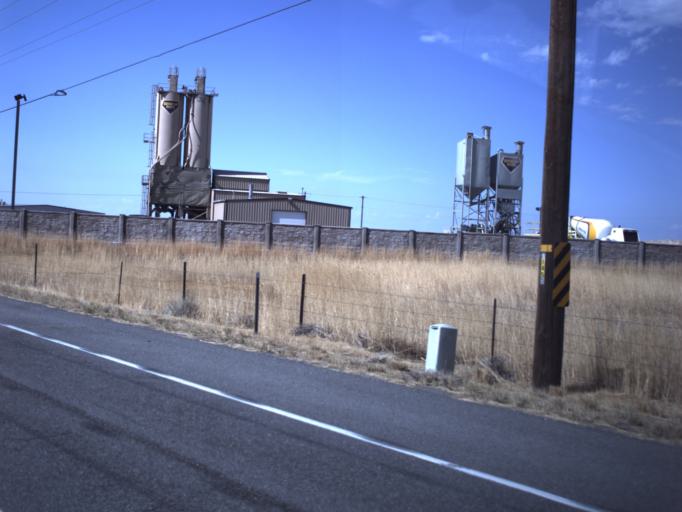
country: US
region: Utah
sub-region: Tooele County
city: Tooele
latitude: 40.5514
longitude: -112.3446
